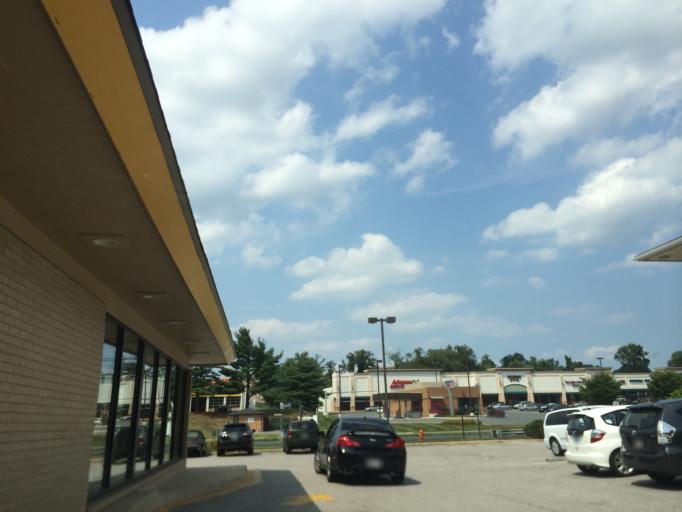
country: US
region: Maryland
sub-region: Howard County
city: Ellicott City
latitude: 39.2766
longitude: -76.8292
